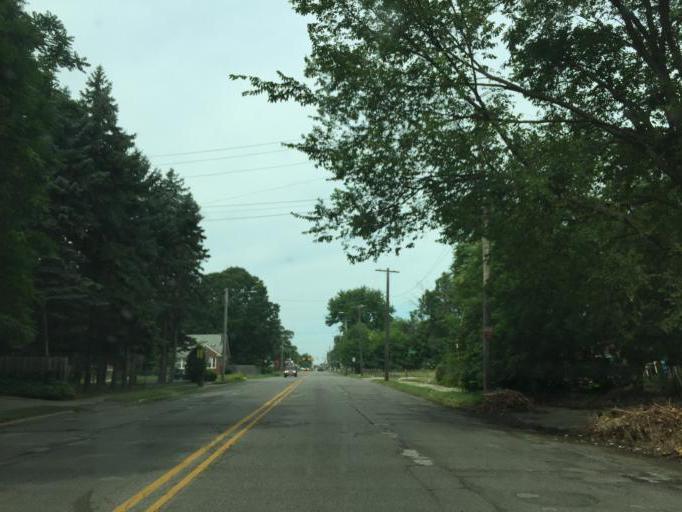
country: US
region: Michigan
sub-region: Wayne County
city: Redford
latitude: 42.4008
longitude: -83.2340
